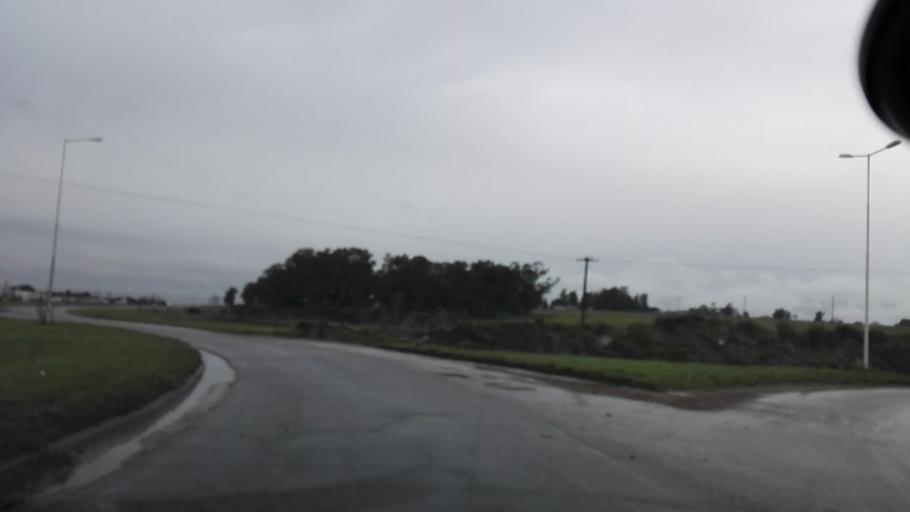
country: AR
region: Buenos Aires
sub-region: Partido de Tandil
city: Tandil
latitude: -37.2977
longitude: -59.1833
